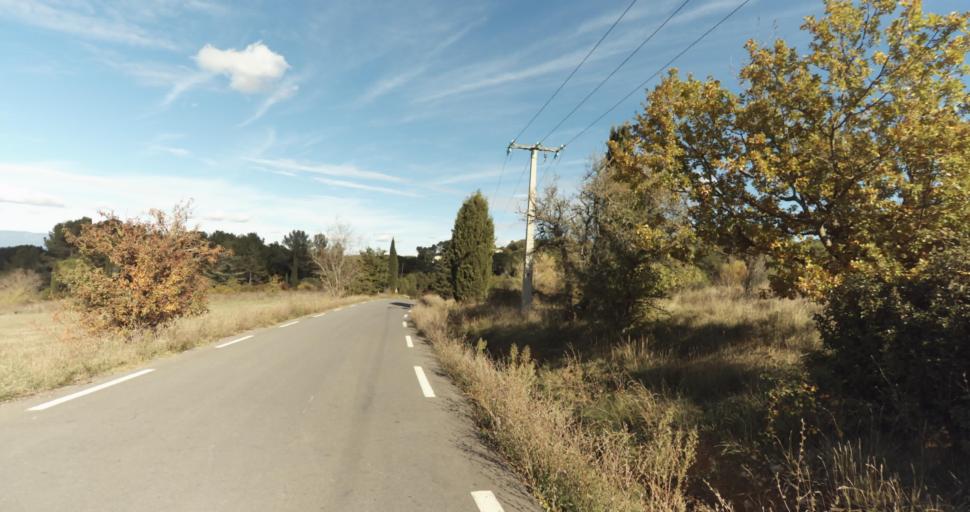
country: FR
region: Provence-Alpes-Cote d'Azur
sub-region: Departement des Bouches-du-Rhone
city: Venelles
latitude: 43.6047
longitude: 5.4886
